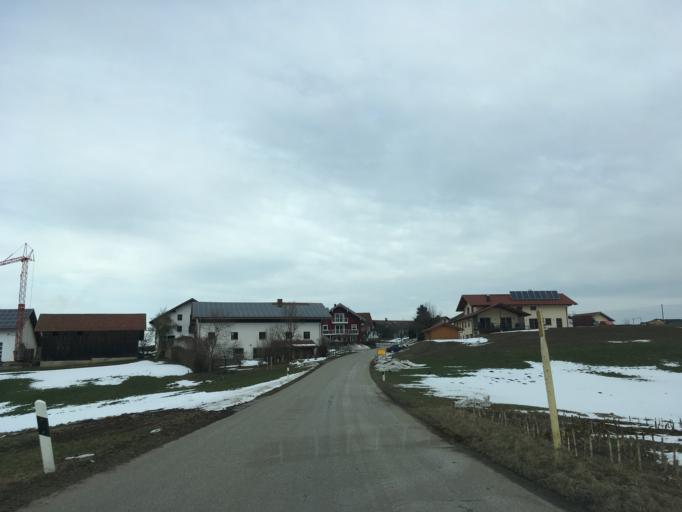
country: DE
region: Bavaria
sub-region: Upper Bavaria
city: Jettenbach
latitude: 48.1253
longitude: 12.3831
